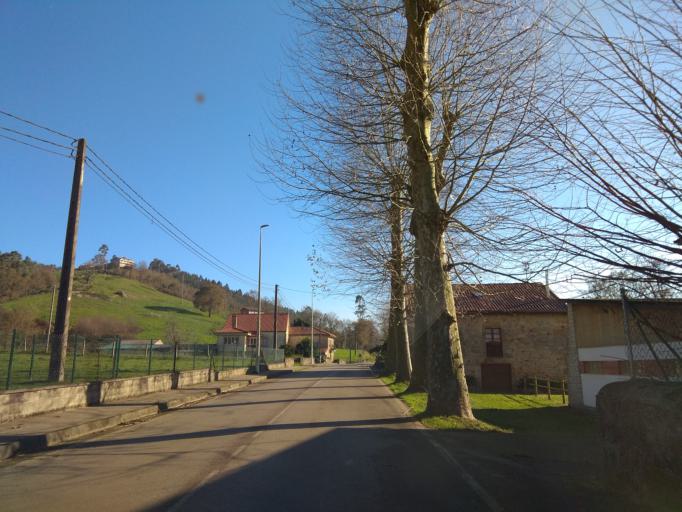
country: ES
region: Cantabria
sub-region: Provincia de Cantabria
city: Entrambasaguas
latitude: 43.3720
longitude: -3.6605
